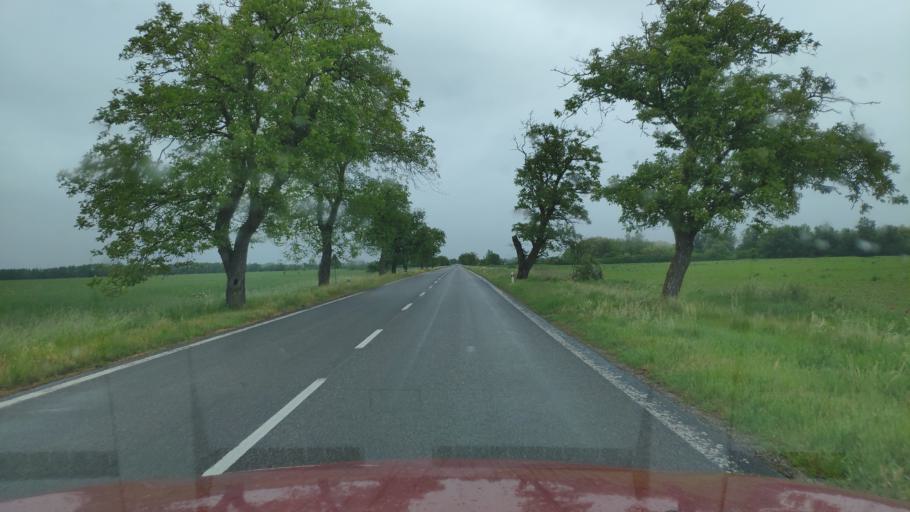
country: HU
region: Borsod-Abauj-Zemplen
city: Karcsa
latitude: 48.4147
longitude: 21.8279
